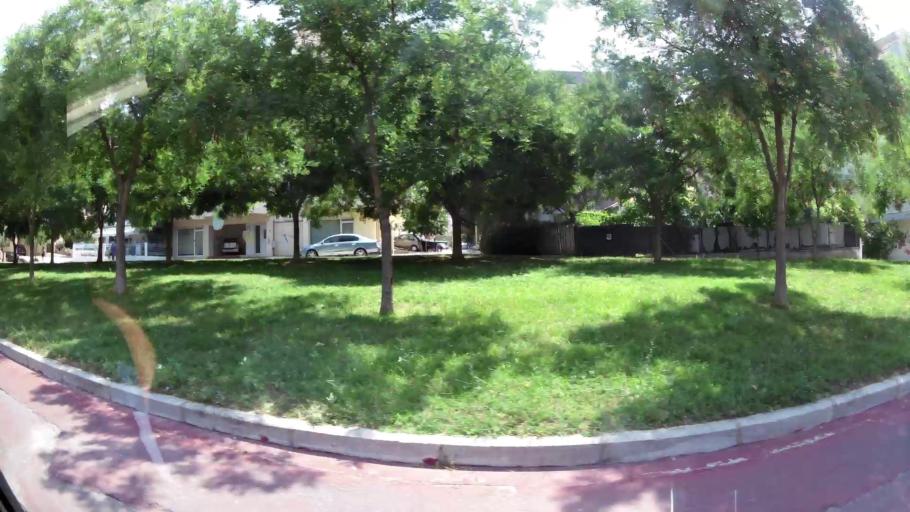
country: GR
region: Central Macedonia
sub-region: Nomos Thessalonikis
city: Evosmos
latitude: 40.6737
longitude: 22.9030
